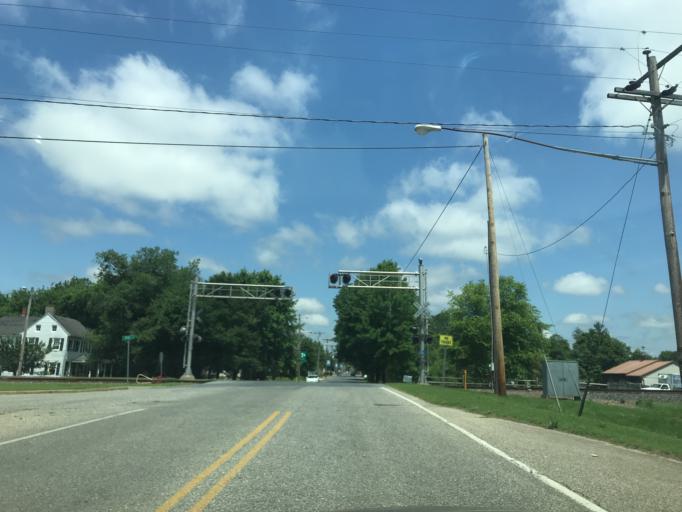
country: US
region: Maryland
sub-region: Caroline County
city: Federalsburg
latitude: 38.6897
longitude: -75.7723
